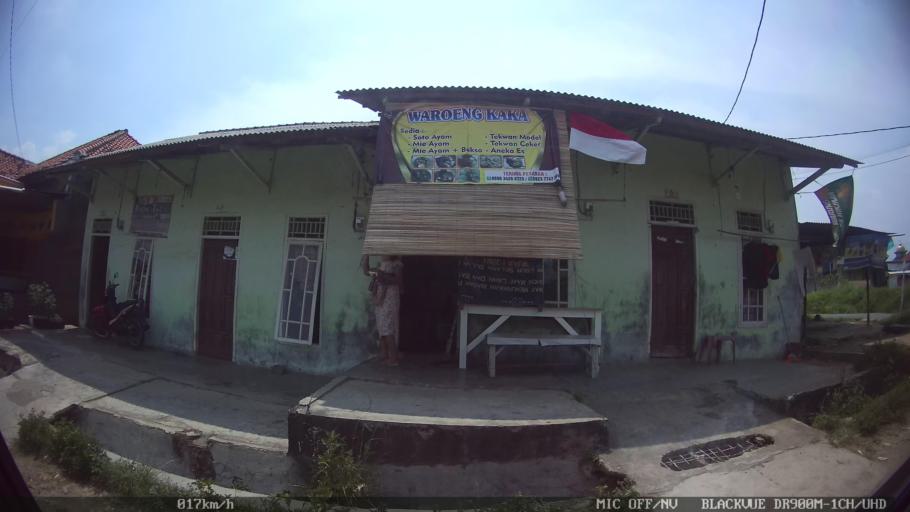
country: ID
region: Lampung
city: Bandarlampung
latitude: -5.4478
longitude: 105.2508
